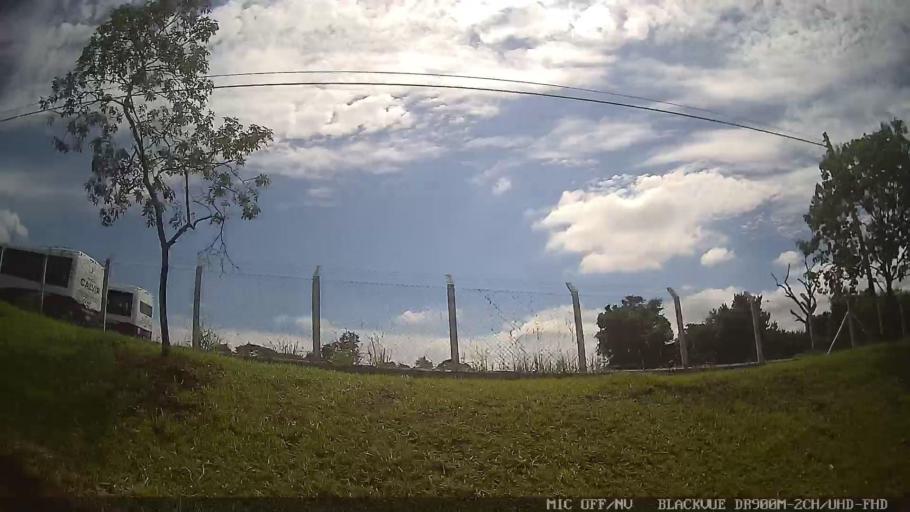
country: BR
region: Sao Paulo
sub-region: Laranjal Paulista
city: Laranjal Paulista
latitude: -23.0811
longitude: -47.7908
